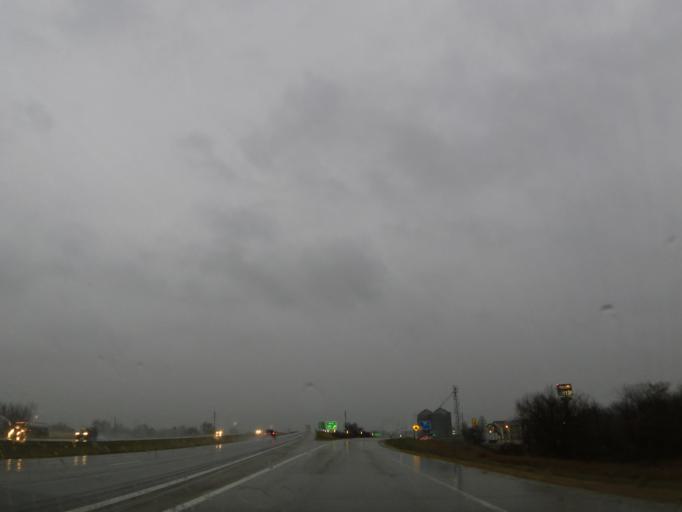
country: US
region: Iowa
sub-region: Cerro Gordo County
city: Clear Lake
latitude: 43.1302
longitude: -93.3559
